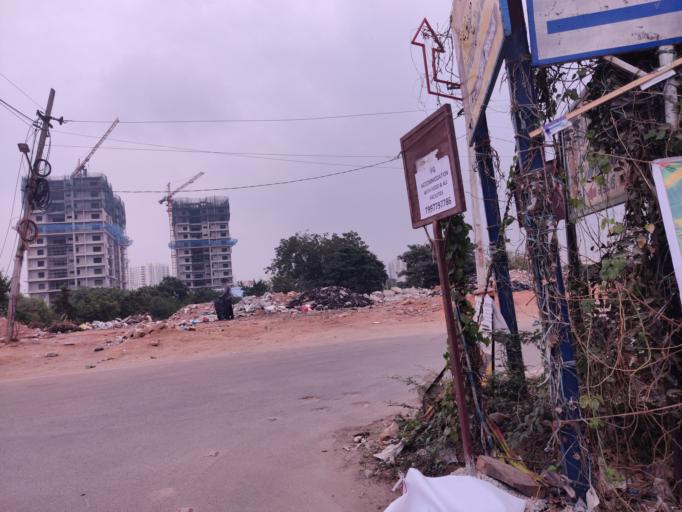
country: IN
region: Telangana
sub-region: Hyderabad
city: Hyderabad
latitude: 17.4088
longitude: 78.3946
